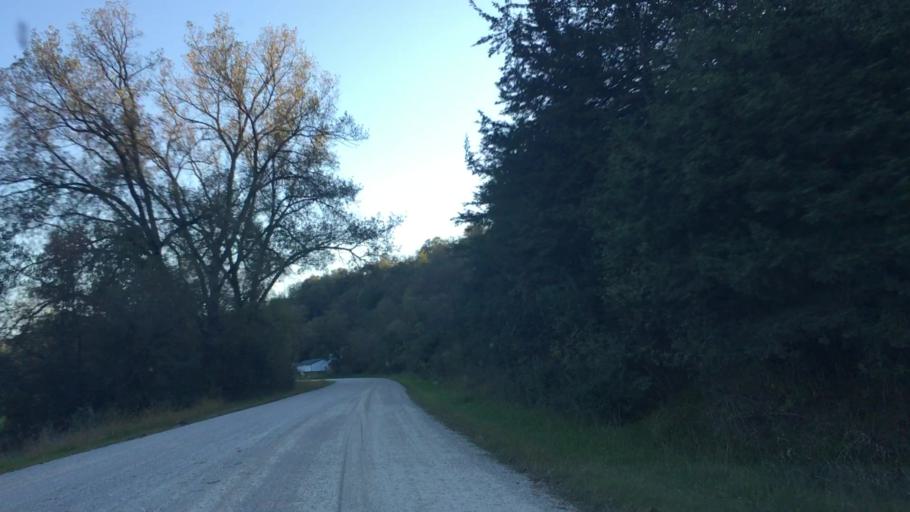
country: US
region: Minnesota
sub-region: Fillmore County
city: Preston
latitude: 43.7613
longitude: -92.0291
